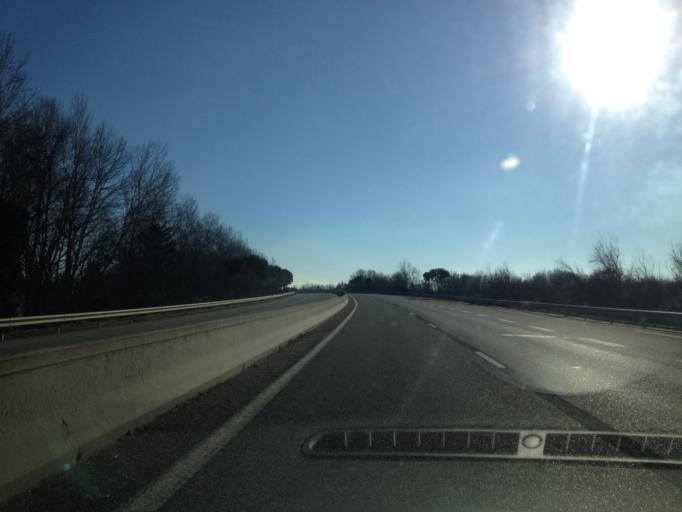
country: FR
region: Provence-Alpes-Cote d'Azur
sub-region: Departement du Vaucluse
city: Sorgues
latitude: 44.0084
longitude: 4.8636
